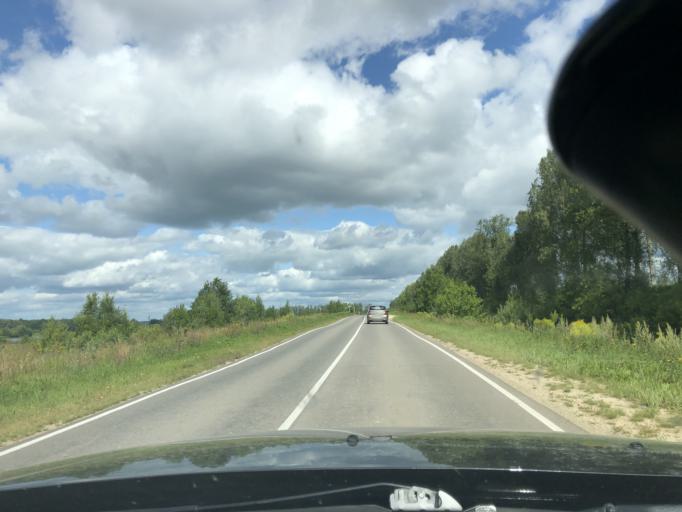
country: RU
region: Tula
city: Yasnogorsk
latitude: 54.4538
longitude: 37.7130
